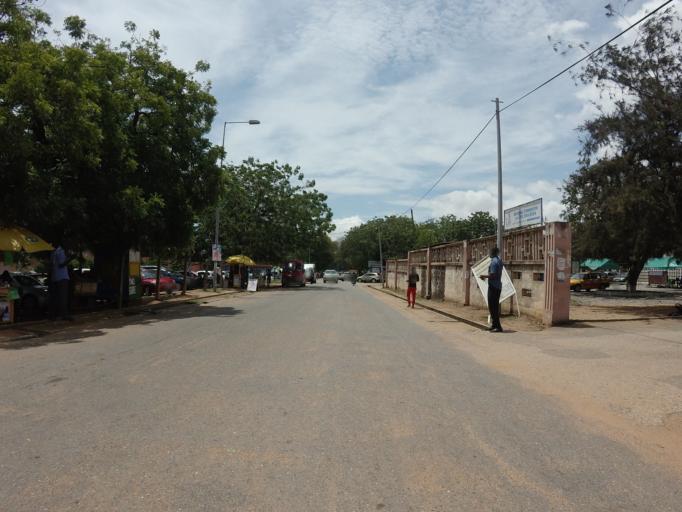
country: GH
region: Greater Accra
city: Accra
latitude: 5.5578
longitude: -0.2063
